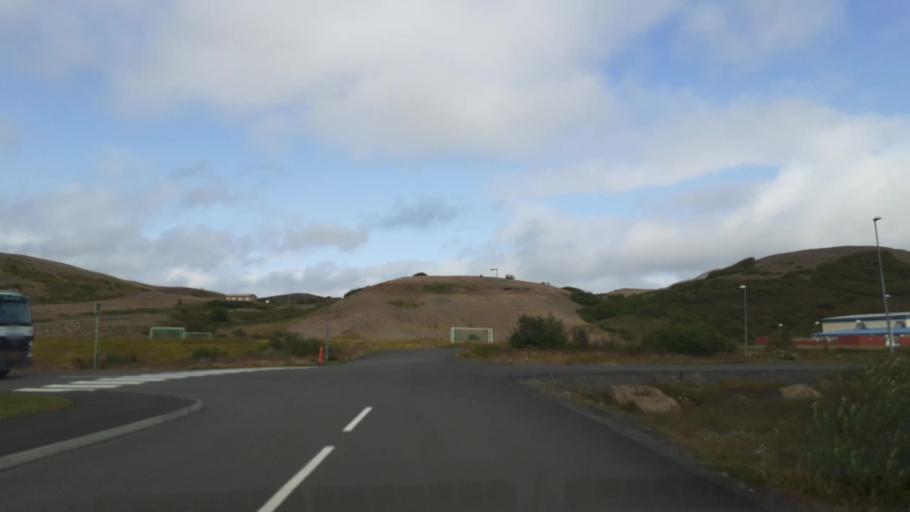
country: IS
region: Northeast
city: Laugar
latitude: 65.6417
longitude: -16.8956
